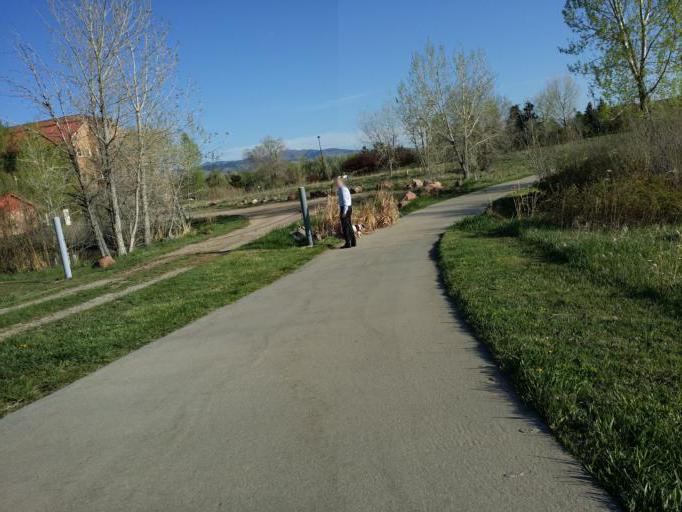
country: US
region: Colorado
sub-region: Boulder County
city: Boulder
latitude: 40.0086
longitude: -105.2457
